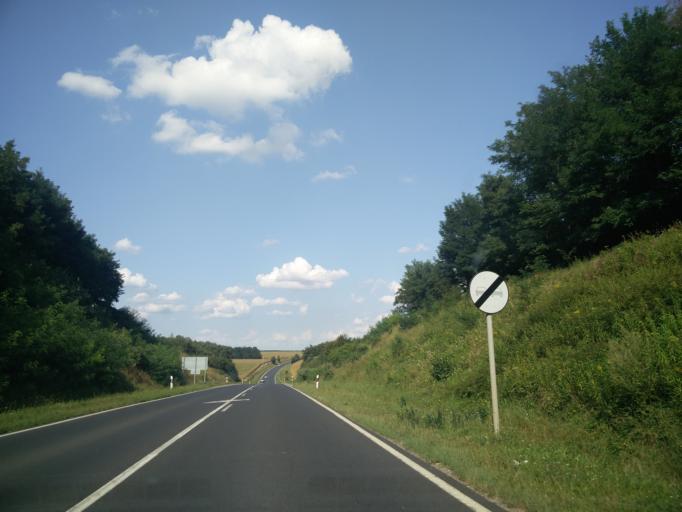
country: HU
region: Zala
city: Zalaegerszeg
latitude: 46.8746
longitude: 16.8050
